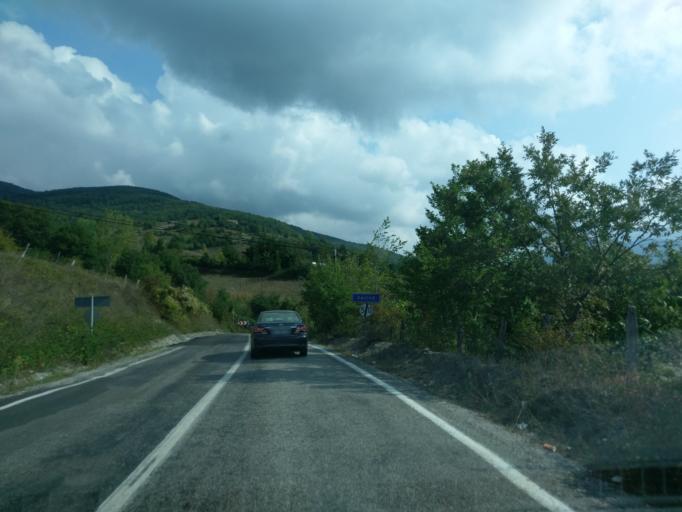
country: TR
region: Sinop
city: Yenikonak
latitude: 41.8766
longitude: 34.5428
